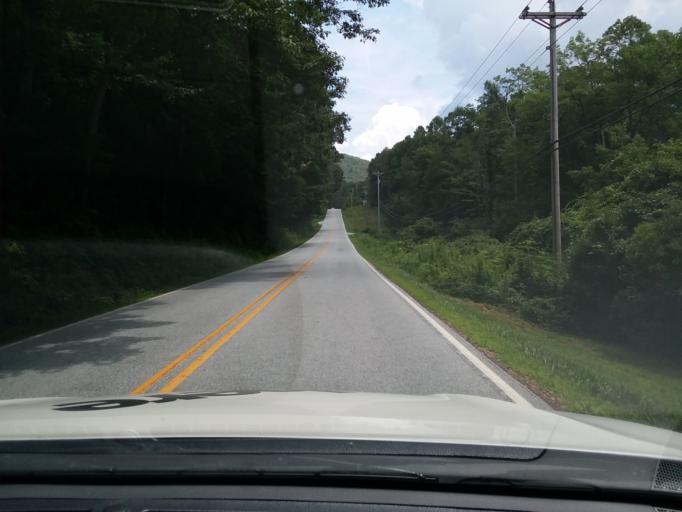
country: US
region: Georgia
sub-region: Rabun County
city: Mountain City
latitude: 35.0236
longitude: -83.2962
